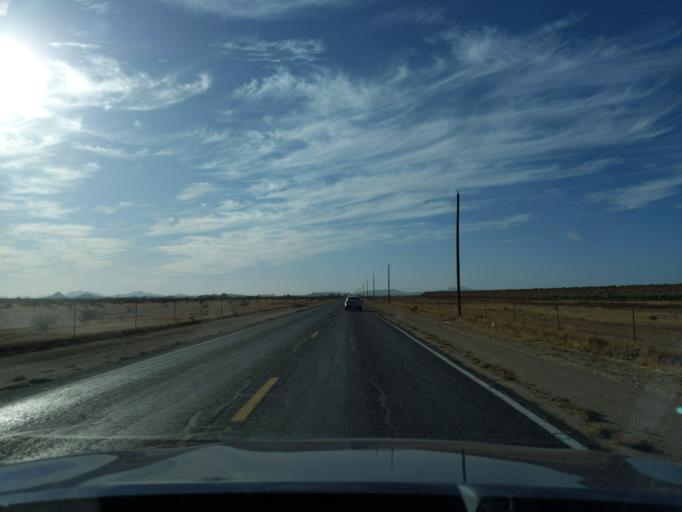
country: US
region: Arizona
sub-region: Pinal County
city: Florence
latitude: 33.1183
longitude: -111.3936
